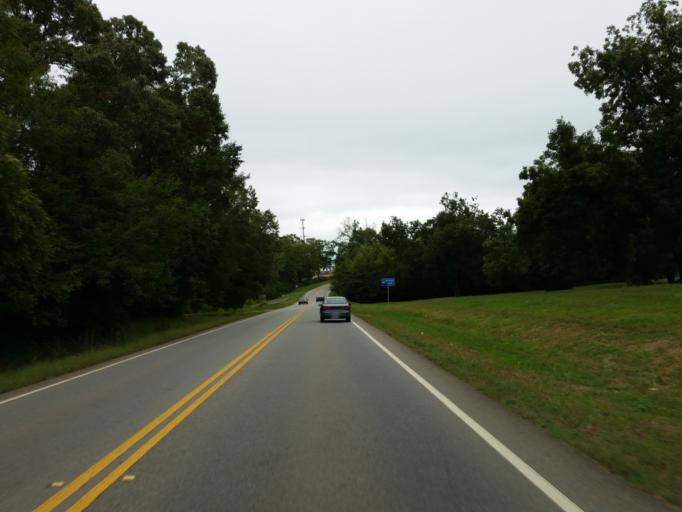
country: US
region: Georgia
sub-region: Peach County
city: Fort Valley
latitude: 32.5642
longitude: -83.8853
